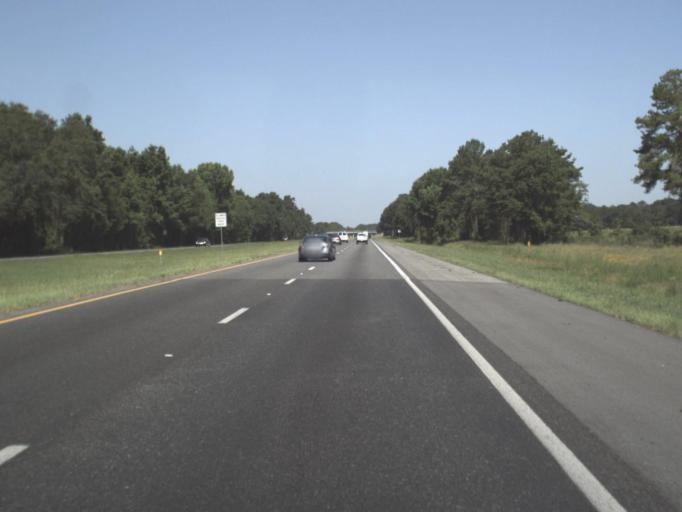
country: US
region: Florida
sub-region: Suwannee County
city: Live Oak
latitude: 30.2948
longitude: -82.8898
